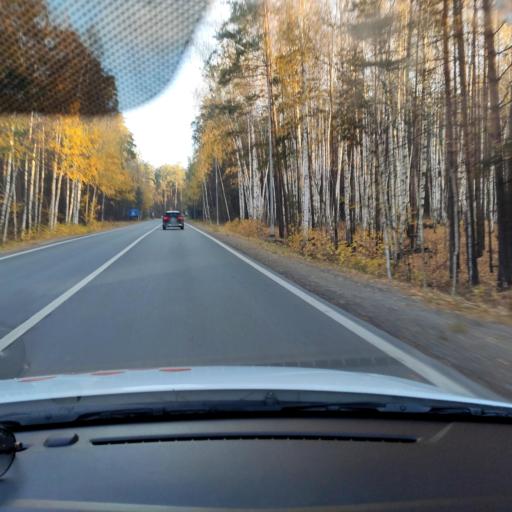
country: RU
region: Tatarstan
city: Verkhniy Uslon
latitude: 55.6377
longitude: 49.0225
